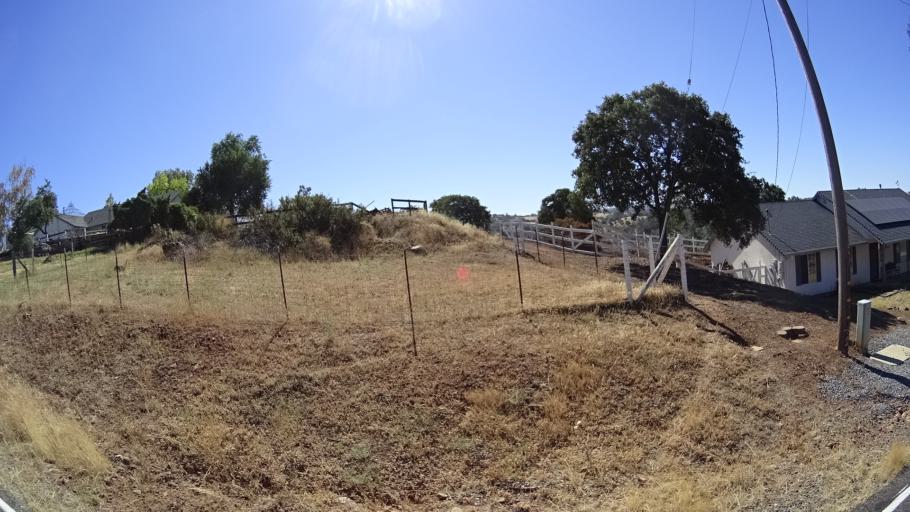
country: US
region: California
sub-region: Calaveras County
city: Rancho Calaveras
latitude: 38.0983
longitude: -120.8559
